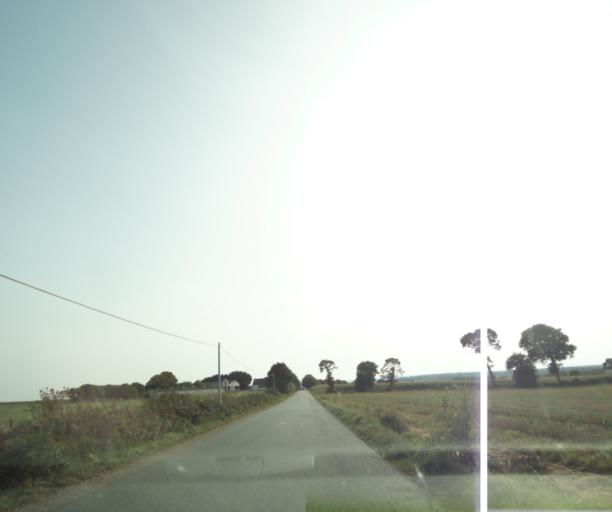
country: FR
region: Brittany
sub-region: Departement des Cotes-d'Armor
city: Jugon-les-Lacs
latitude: 48.4246
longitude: -2.3080
